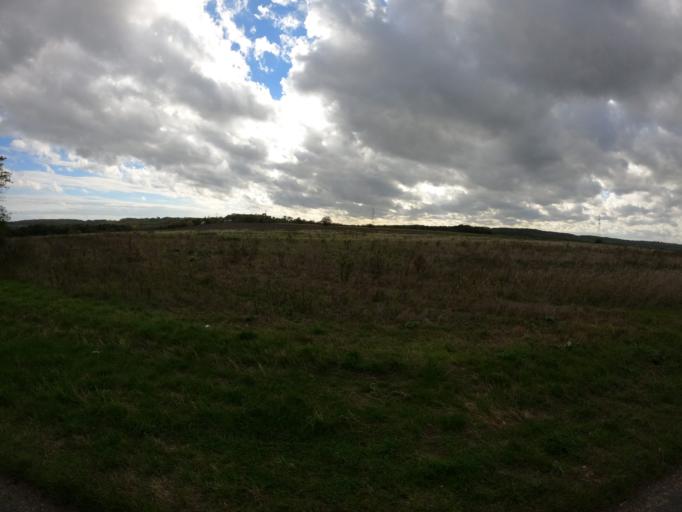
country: FR
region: Ile-de-France
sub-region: Departement de Seine-et-Marne
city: Chalifert
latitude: 48.9125
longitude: 2.7701
